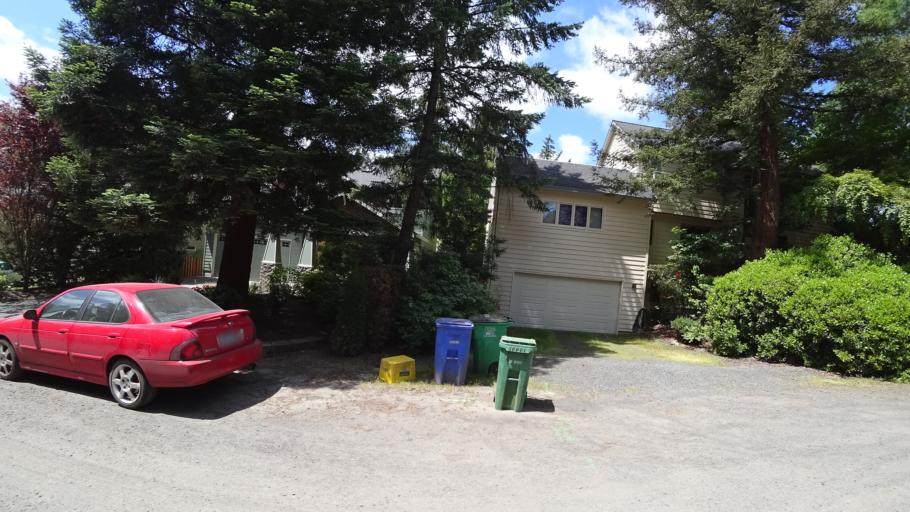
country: US
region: Oregon
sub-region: Washington County
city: Garden Home-Whitford
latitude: 45.4580
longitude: -122.7201
